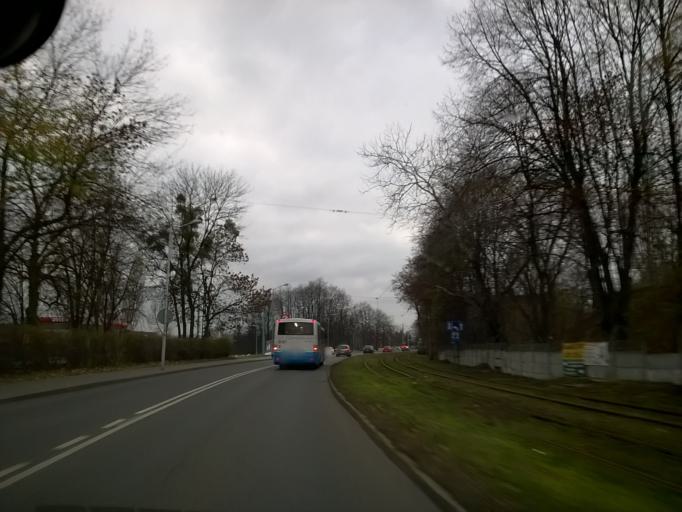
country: PL
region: Silesian Voivodeship
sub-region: Swietochlowice
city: Swietochlowice
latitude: 50.2839
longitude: 18.9235
